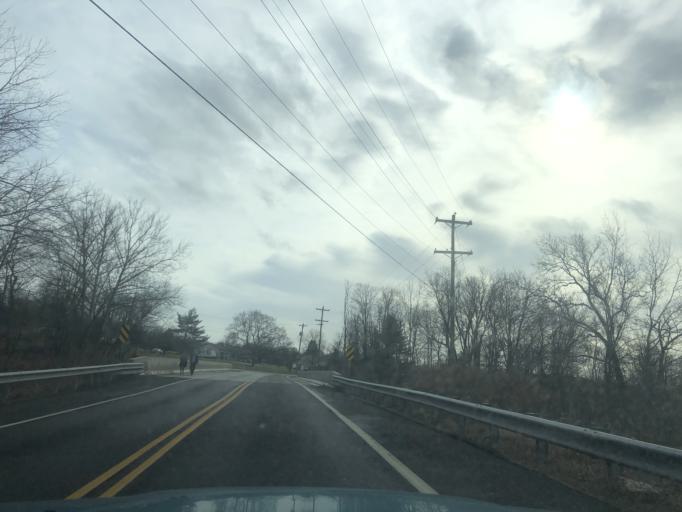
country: US
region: Pennsylvania
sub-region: Montgomery County
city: Harleysville
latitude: 40.2740
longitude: -75.4159
